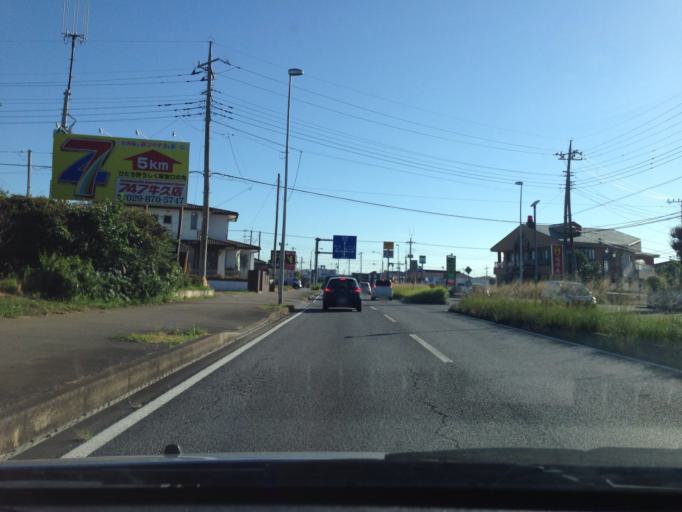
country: JP
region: Ibaraki
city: Naka
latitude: 36.0399
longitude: 140.1770
